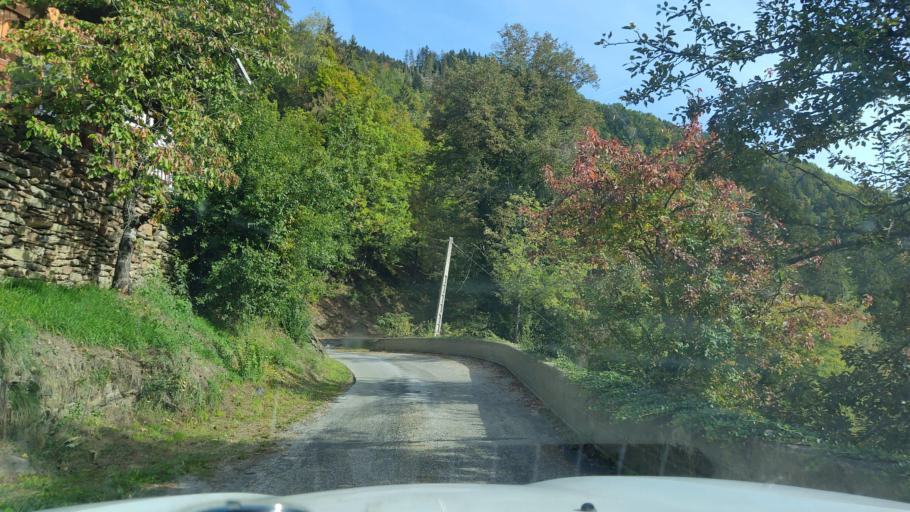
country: FR
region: Rhone-Alpes
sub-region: Departement de la Savoie
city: Beaufort
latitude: 45.7223
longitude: 6.5010
